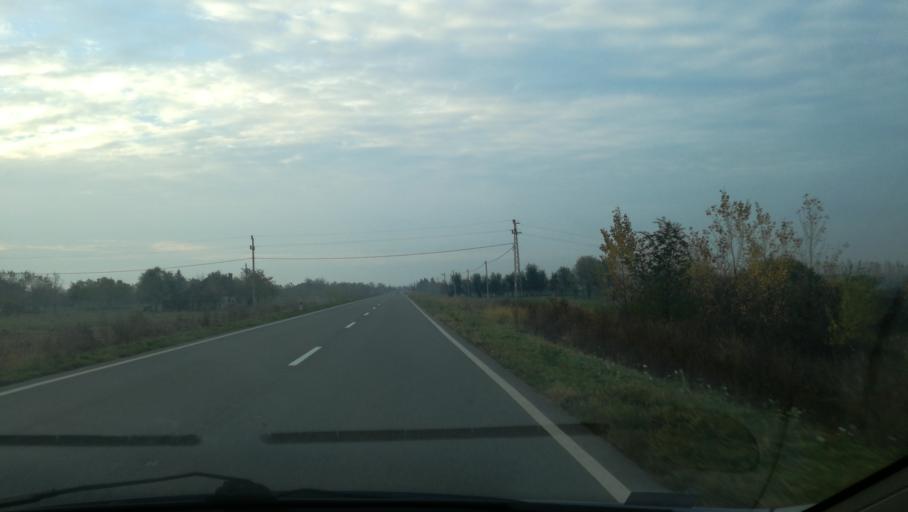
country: RS
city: Banatska Topola
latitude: 45.6907
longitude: 20.4225
